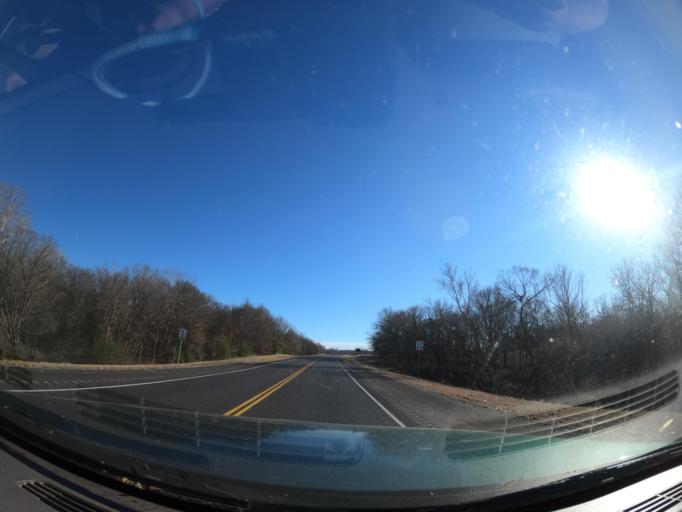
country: US
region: Oklahoma
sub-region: McIntosh County
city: Eufaula
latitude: 35.2645
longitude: -95.5810
